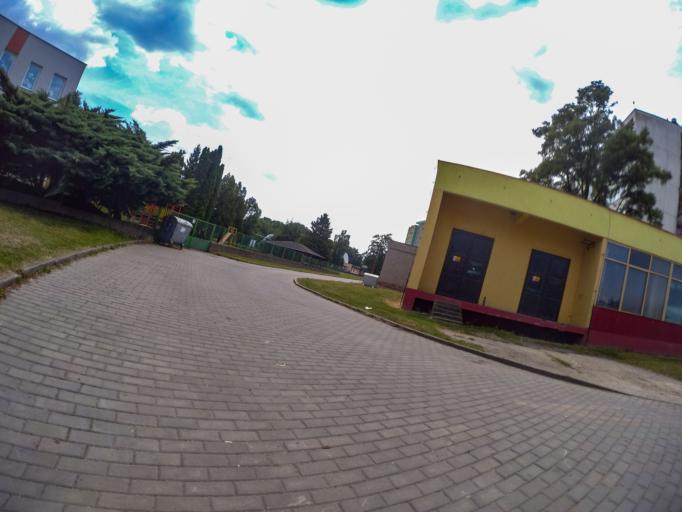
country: CZ
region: Central Bohemia
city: Neratovice
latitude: 50.2533
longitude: 14.5212
